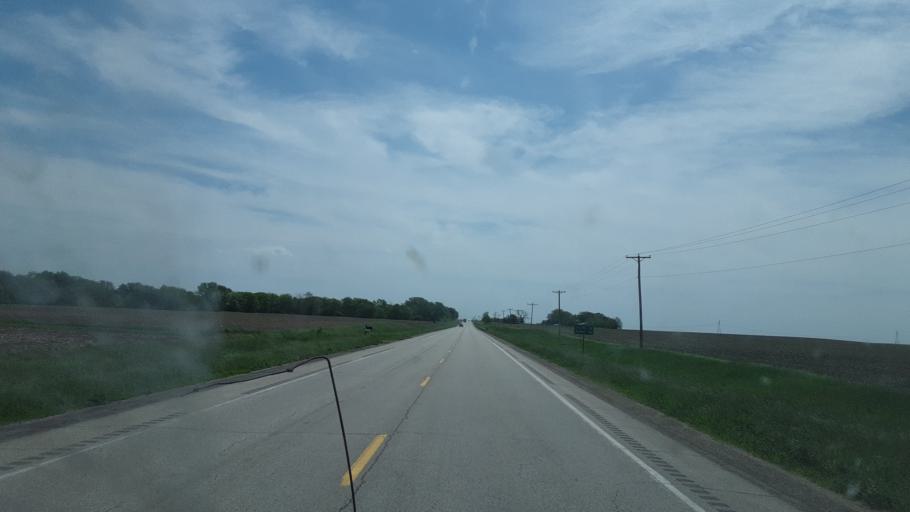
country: US
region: Illinois
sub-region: McLean County
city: Heyworth
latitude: 40.3122
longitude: -88.9594
